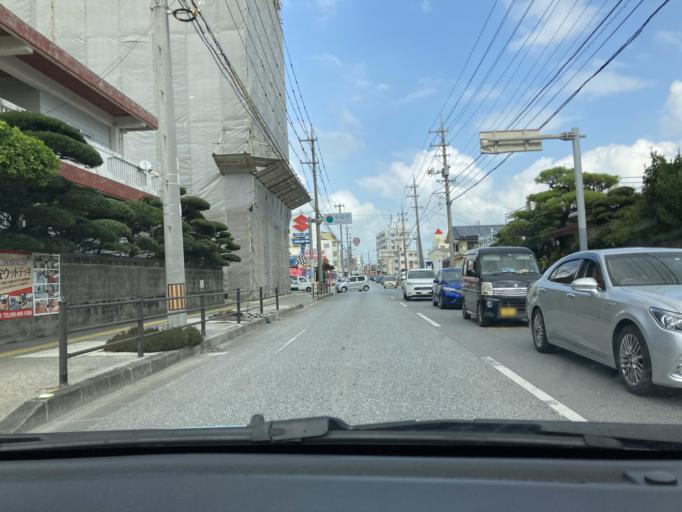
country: JP
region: Okinawa
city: Ginowan
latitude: 26.2423
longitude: 127.7664
